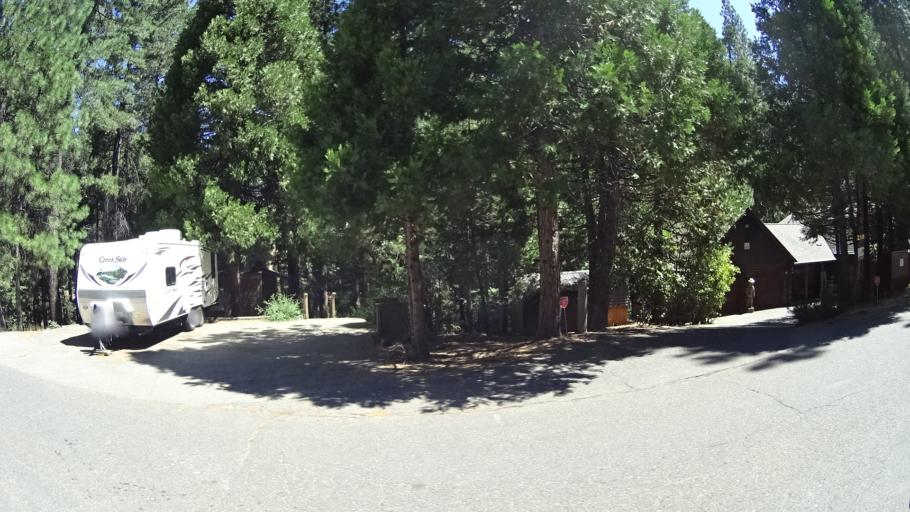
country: US
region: California
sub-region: Calaveras County
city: Arnold
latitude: 38.2286
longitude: -120.3447
